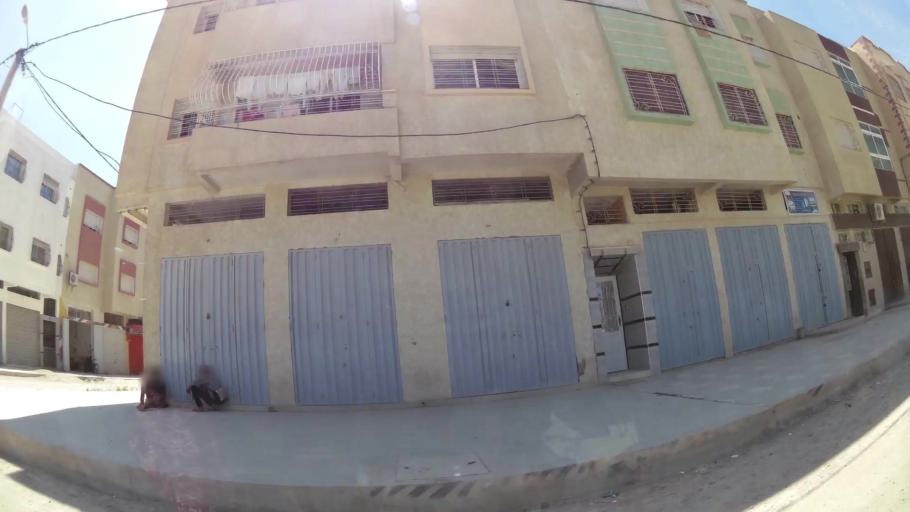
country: MA
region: Fes-Boulemane
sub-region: Fes
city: Fes
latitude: 34.0267
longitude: -5.0447
